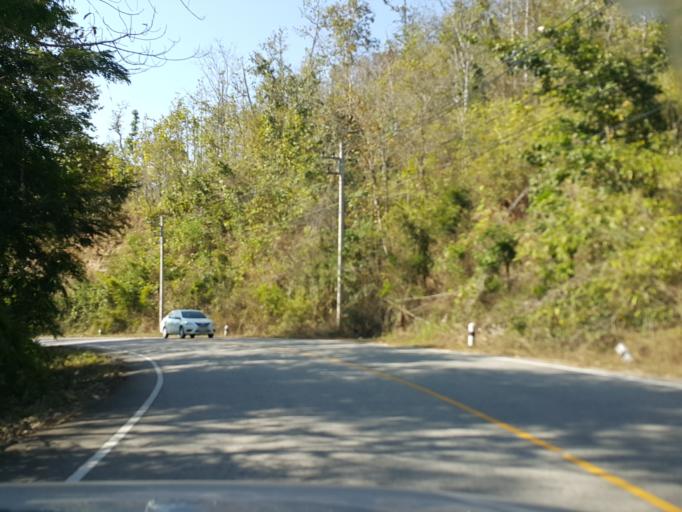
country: TH
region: Chiang Mai
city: Mae Wang
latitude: 18.6200
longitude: 98.7264
